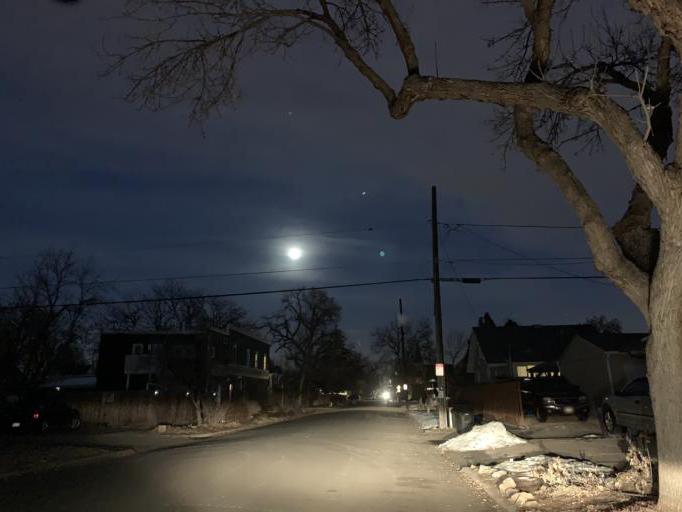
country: US
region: Colorado
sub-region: Jefferson County
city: Edgewater
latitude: 39.7748
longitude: -105.0517
